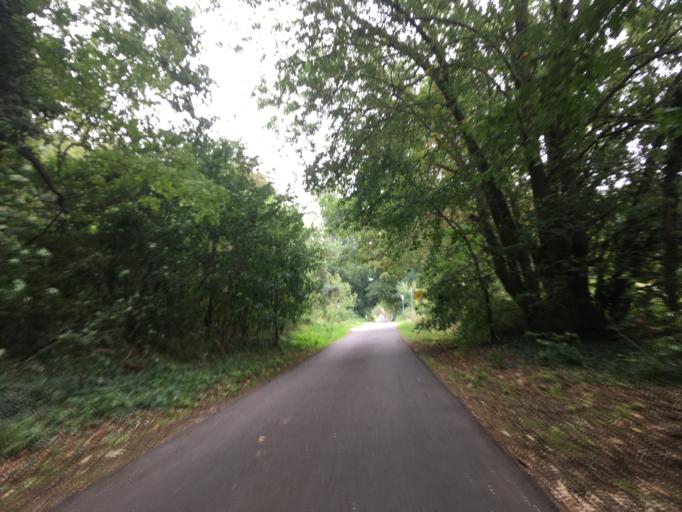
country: DE
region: Brandenburg
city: Gransee
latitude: 53.0578
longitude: 13.2188
